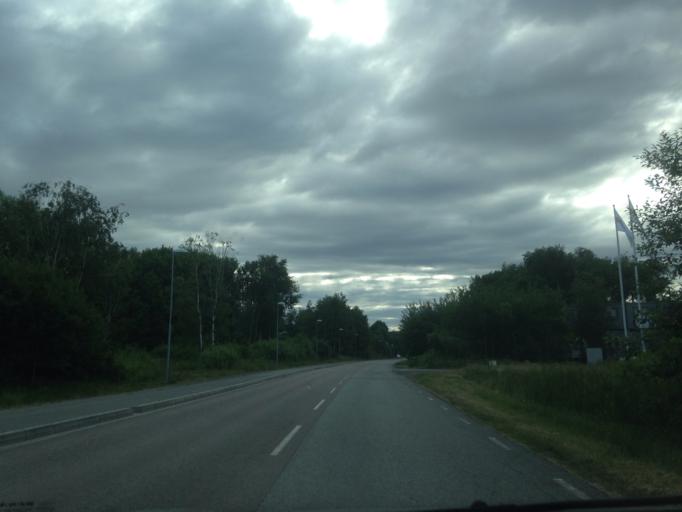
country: SE
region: Vaestra Goetaland
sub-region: Goteborg
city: Torslanda
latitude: 57.7634
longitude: 11.8147
